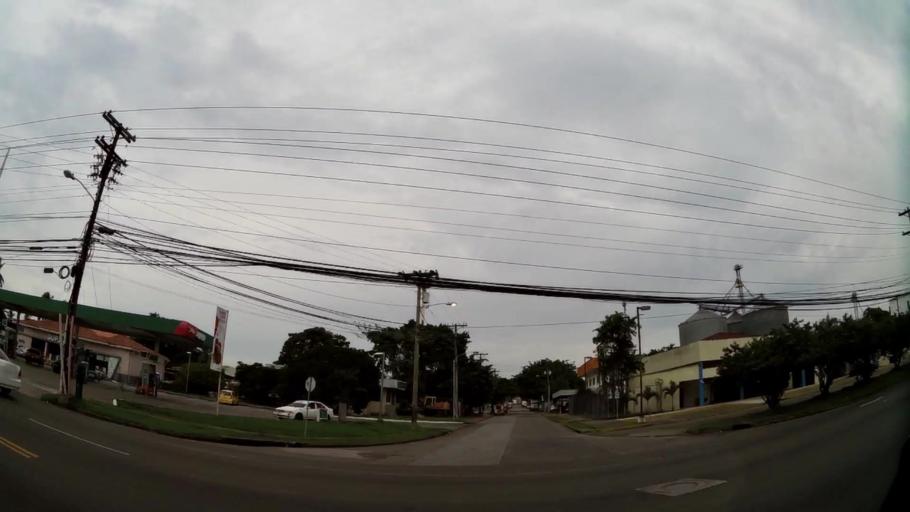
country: PA
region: Panama
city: San Miguelito
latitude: 9.0361
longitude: -79.4717
